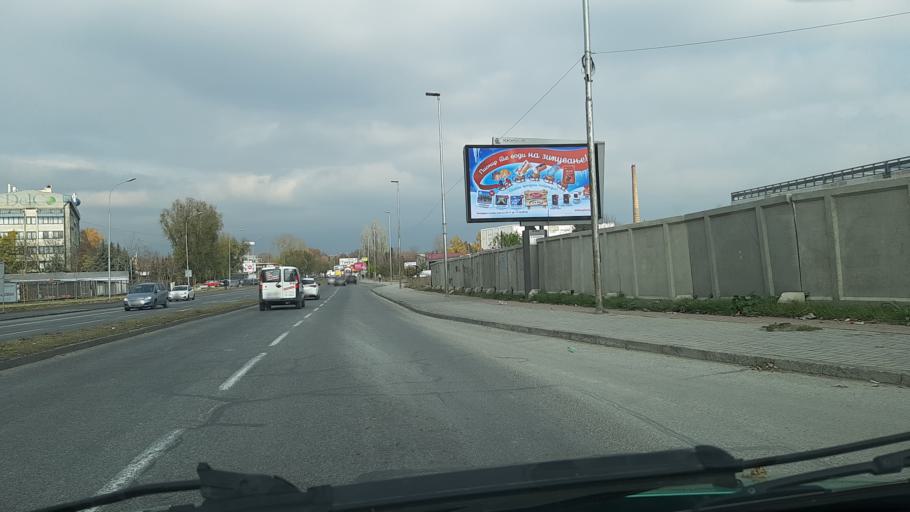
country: MK
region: Kisela Voda
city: Usje
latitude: 41.9933
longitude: 21.4753
